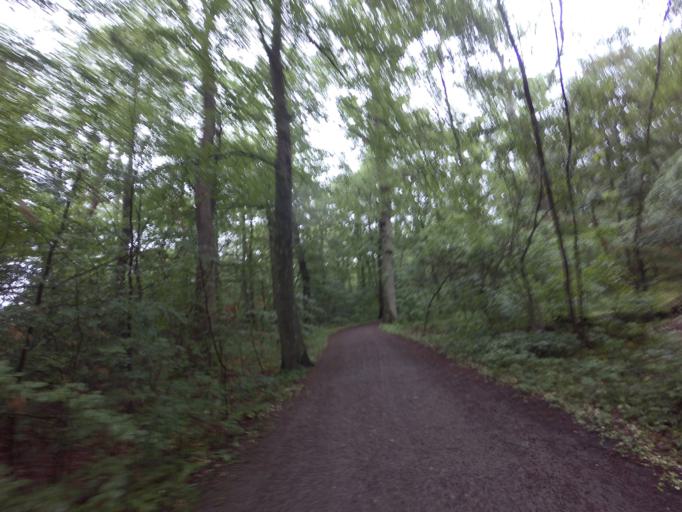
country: SE
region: Skane
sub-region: Helsingborg
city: Odakra
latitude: 56.0885
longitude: 12.7284
